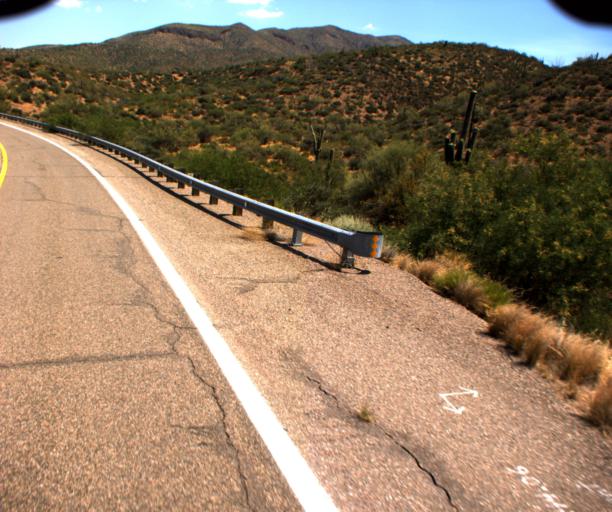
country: US
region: Arizona
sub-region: Gila County
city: Tonto Basin
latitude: 33.6680
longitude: -111.1399
